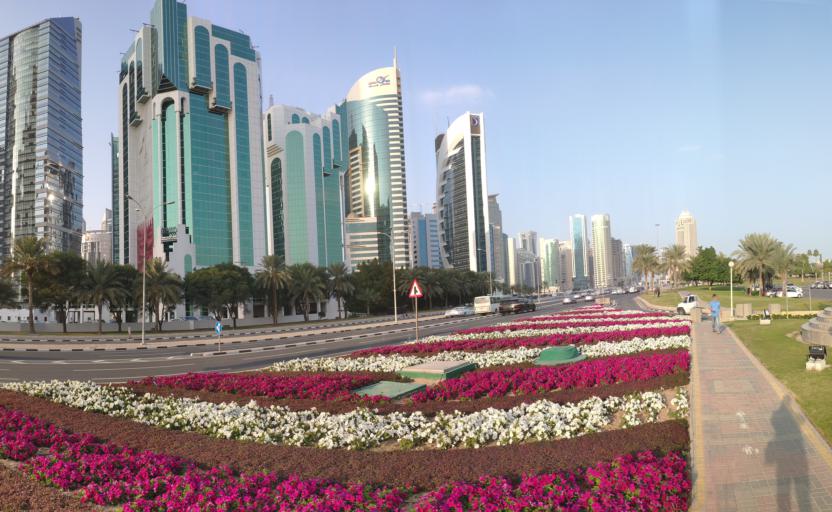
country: QA
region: Baladiyat ad Dawhah
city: Doha
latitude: 25.3176
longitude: 51.5306
